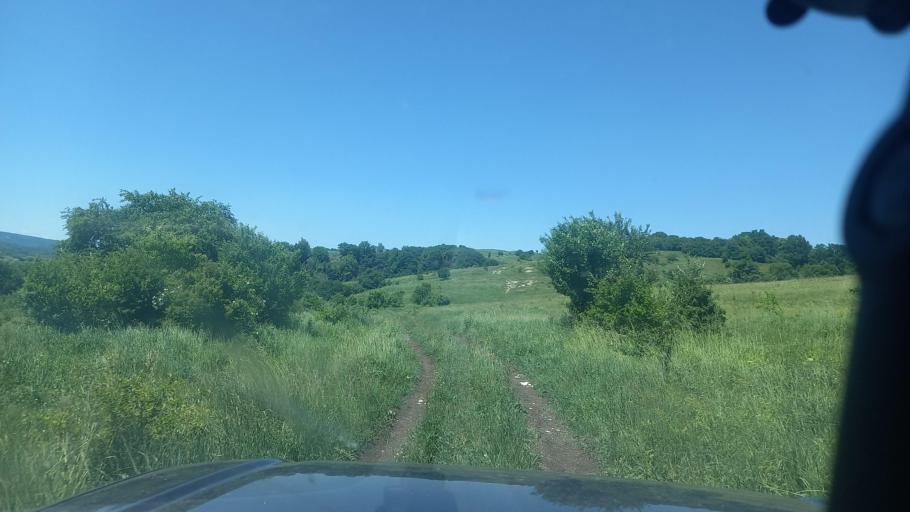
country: RU
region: Karachayevo-Cherkesiya
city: Pregradnaya
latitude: 44.1095
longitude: 41.1253
